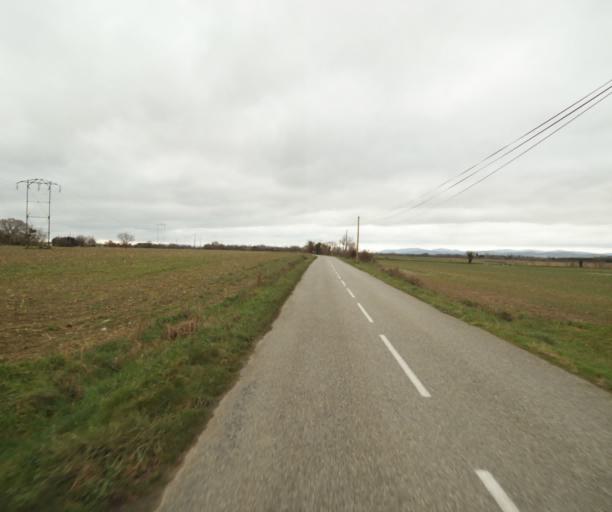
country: FR
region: Midi-Pyrenees
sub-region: Departement de l'Ariege
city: Mazeres
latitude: 43.1906
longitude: 1.6335
